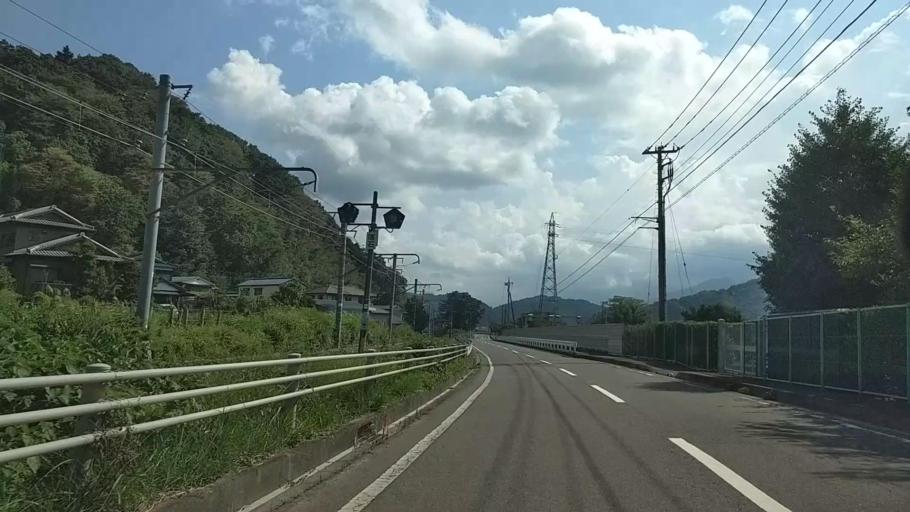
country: JP
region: Shizuoka
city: Fujinomiya
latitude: 35.3774
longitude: 138.4522
